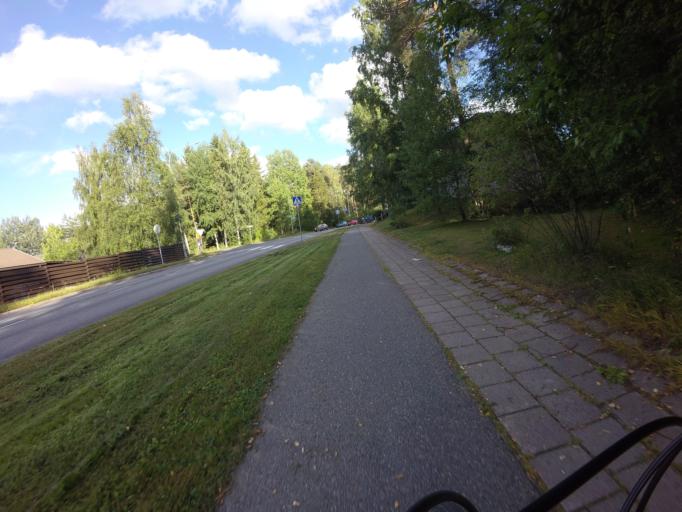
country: FI
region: Varsinais-Suomi
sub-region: Turku
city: Vahto
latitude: 60.5456
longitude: 22.3571
